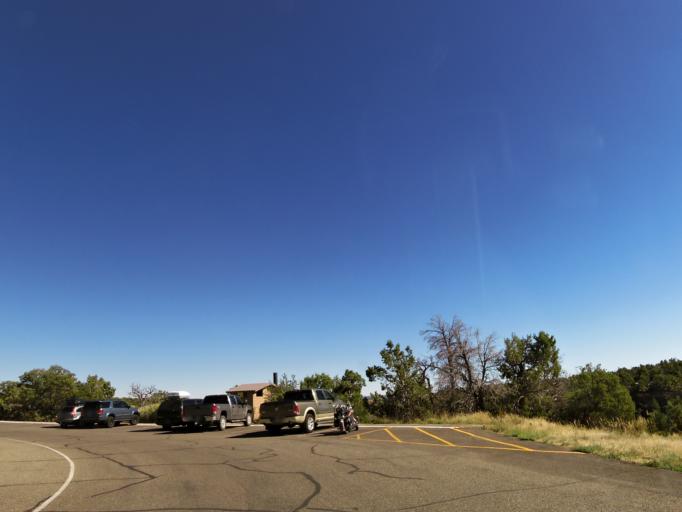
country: US
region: Colorado
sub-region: Montezuma County
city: Cortez
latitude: 37.1650
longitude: -108.4766
